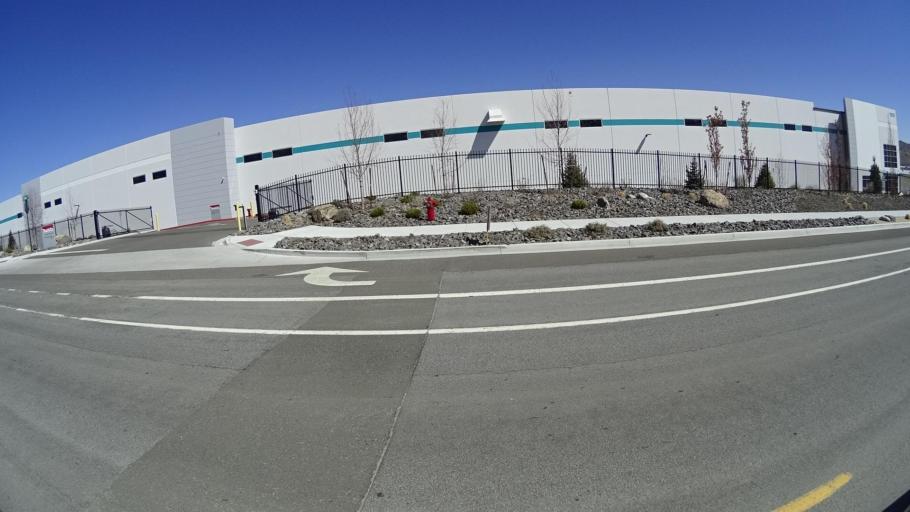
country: US
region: Nevada
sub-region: Washoe County
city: Lemmon Valley
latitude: 39.6499
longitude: -119.8694
